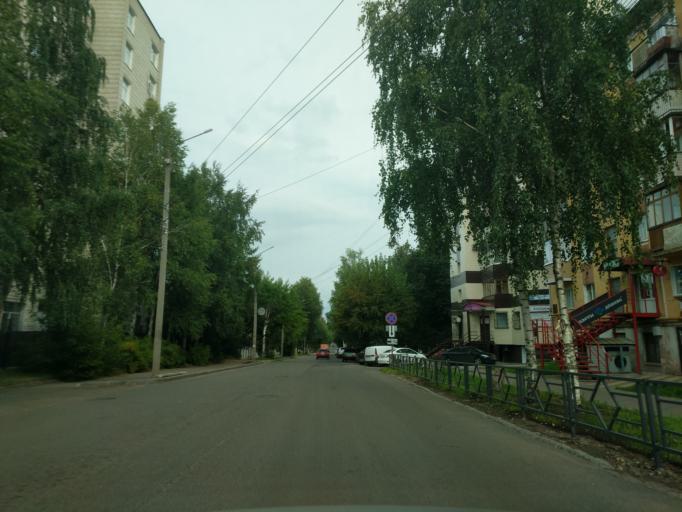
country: RU
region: Kirov
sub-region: Kirovo-Chepetskiy Rayon
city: Kirov
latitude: 58.5963
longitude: 49.6819
